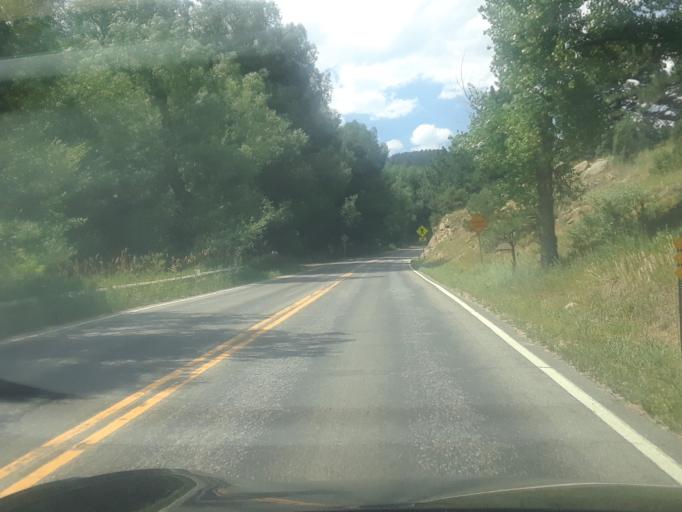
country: US
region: Colorado
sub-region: Boulder County
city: Boulder
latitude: 40.0263
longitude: -105.3128
